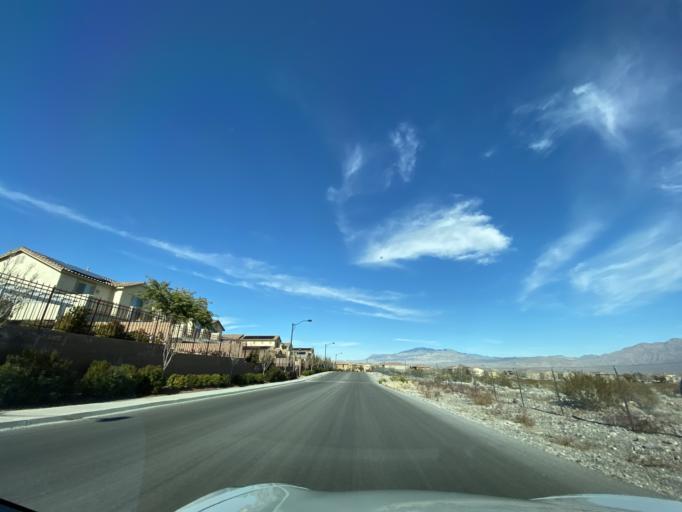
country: US
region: Nevada
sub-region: Clark County
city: Summerlin South
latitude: 36.2975
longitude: -115.3265
